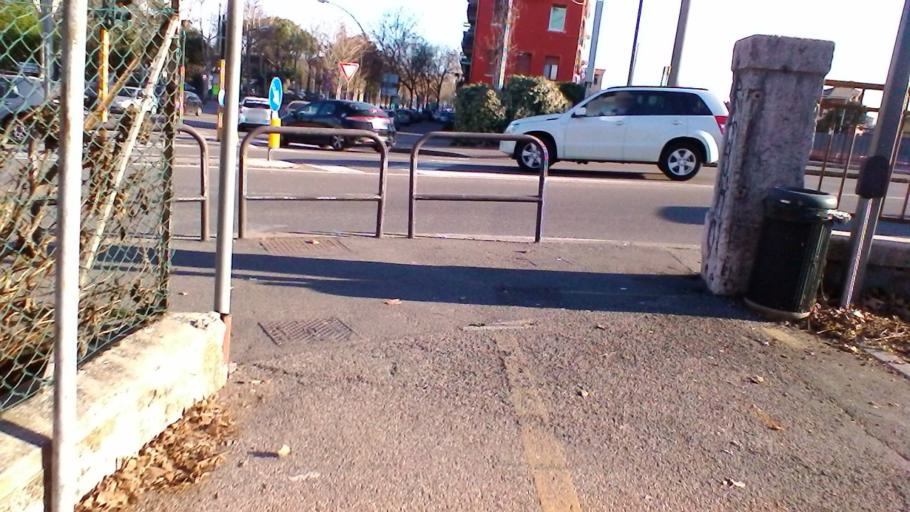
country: IT
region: Veneto
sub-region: Provincia di Verona
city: Verona
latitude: 45.4405
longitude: 10.9737
